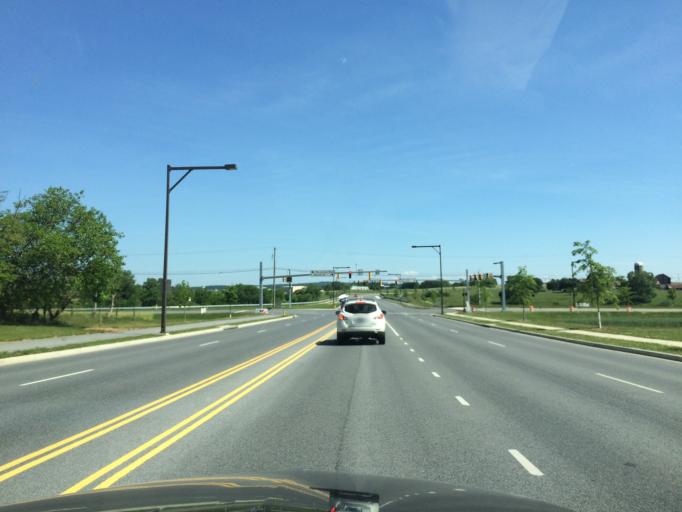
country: US
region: Maryland
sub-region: Frederick County
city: Frederick
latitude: 39.4274
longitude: -77.3864
